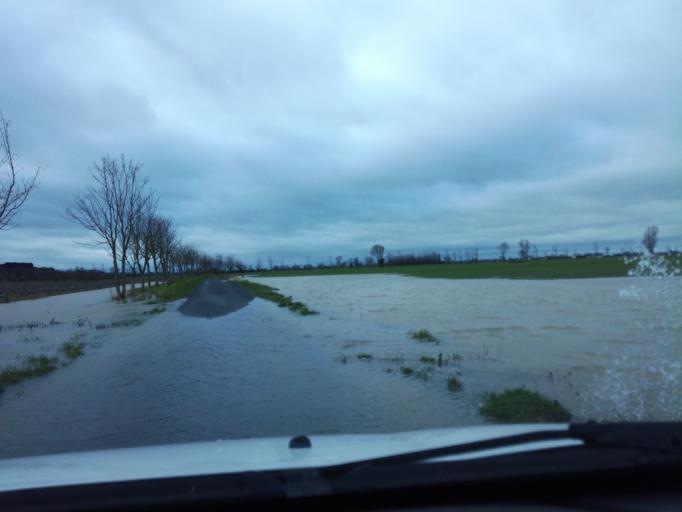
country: FR
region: Brittany
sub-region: Departement d'Ille-et-Vilaine
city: Saint-Broladre
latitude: 48.5852
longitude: -1.6805
